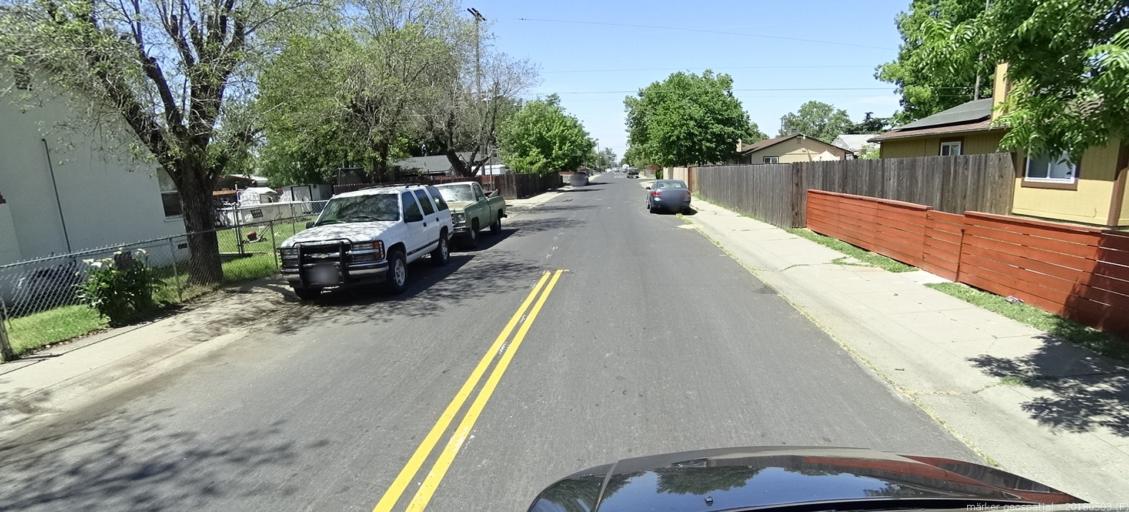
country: US
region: California
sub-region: Sacramento County
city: Rio Linda
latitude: 38.6382
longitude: -121.4245
